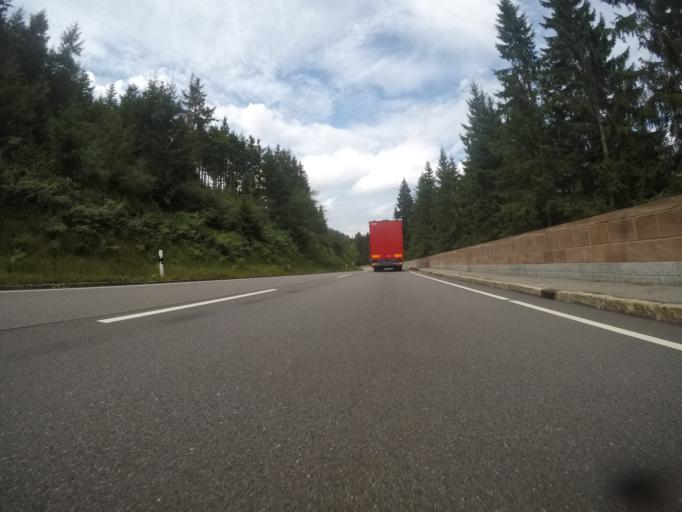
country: DE
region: Baden-Wuerttemberg
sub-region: Freiburg Region
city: Seebach
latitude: 48.5585
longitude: 8.2170
